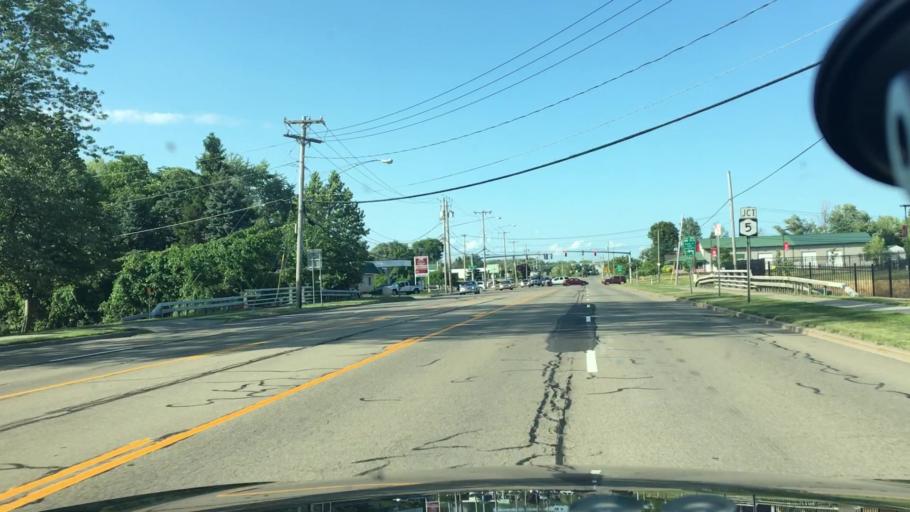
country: US
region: New York
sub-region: Erie County
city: Blasdell
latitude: 42.7711
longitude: -78.8618
